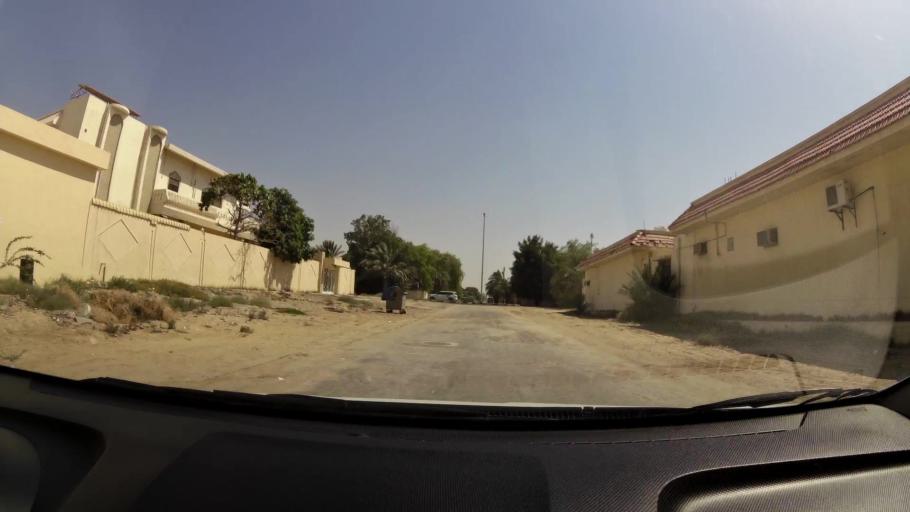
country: AE
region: Ajman
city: Ajman
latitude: 25.4122
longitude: 55.4794
